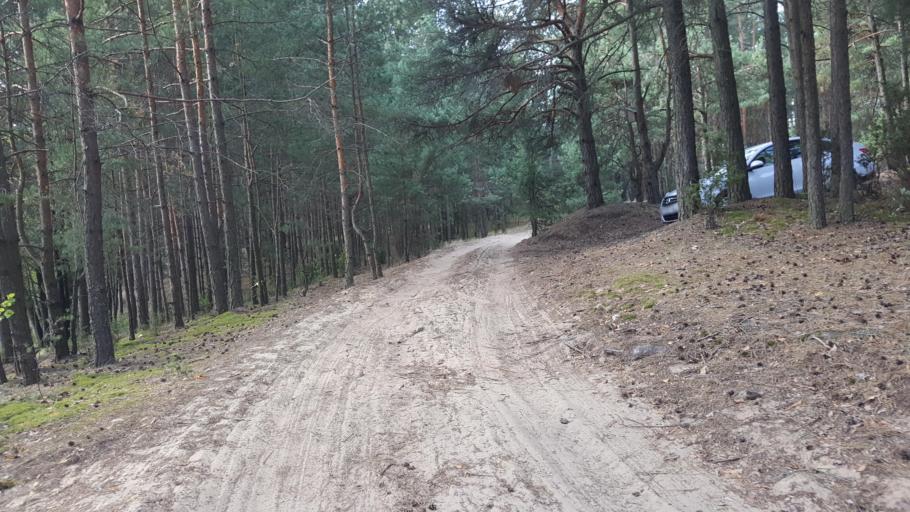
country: BY
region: Brest
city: Ivatsevichy
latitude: 52.7929
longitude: 25.5544
